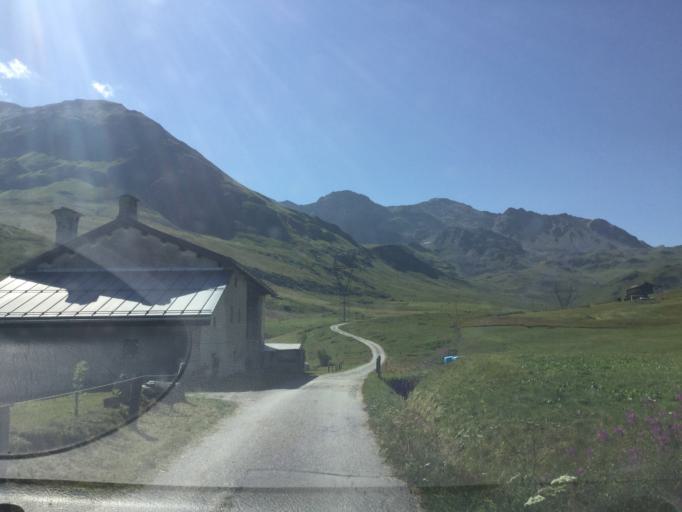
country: CH
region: Grisons
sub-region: Maloja District
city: Silvaplana
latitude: 46.4587
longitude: 9.6562
